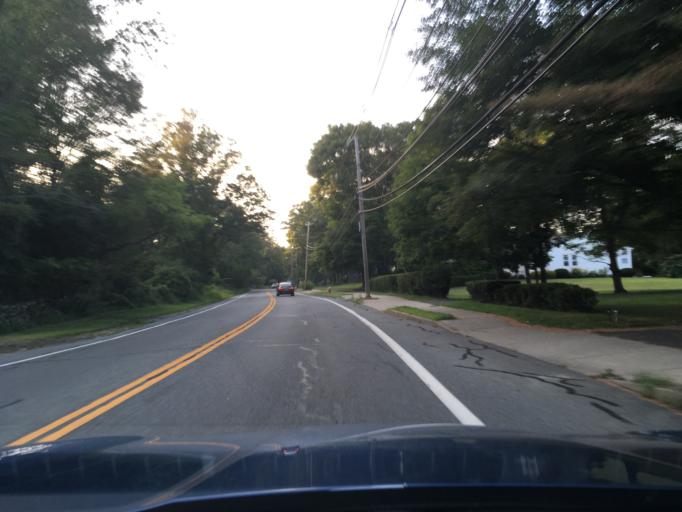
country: US
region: Rhode Island
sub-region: Washington County
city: North Kingstown
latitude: 41.5711
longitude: -71.4613
